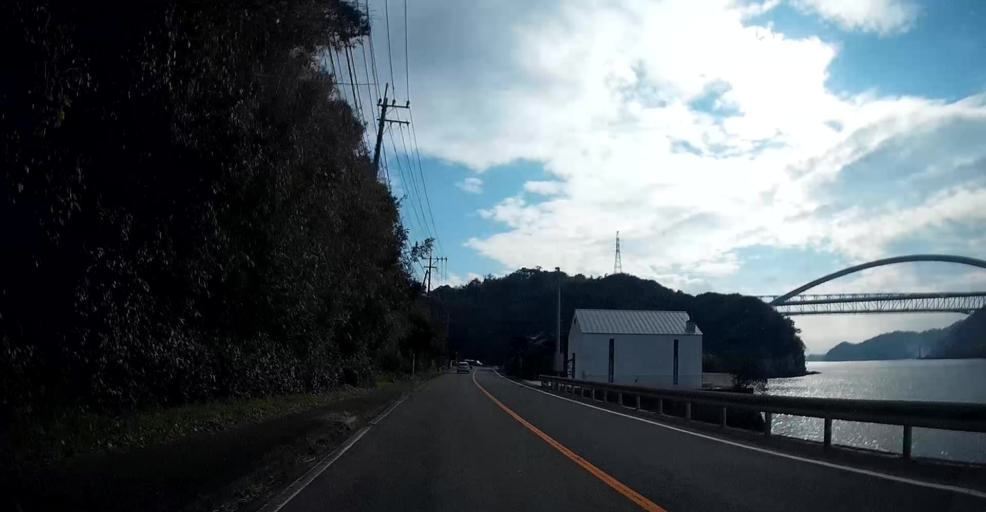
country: JP
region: Kumamoto
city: Yatsushiro
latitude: 32.6146
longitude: 130.4622
